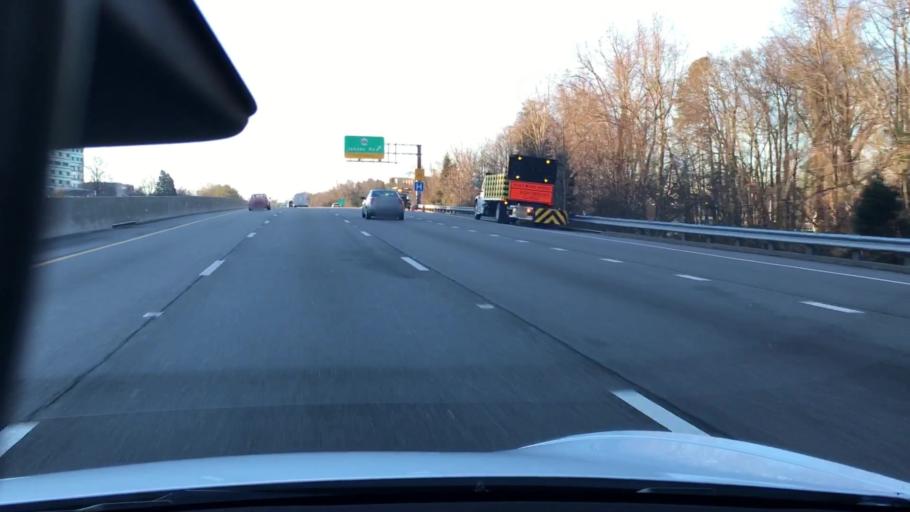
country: US
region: Virginia
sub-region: Chesterfield County
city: Bon Air
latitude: 37.5175
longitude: -77.5284
